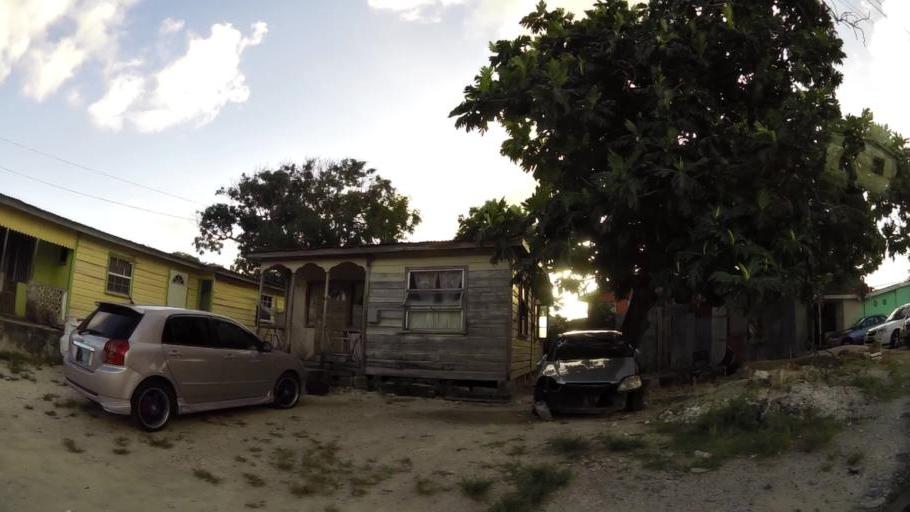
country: BB
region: Saint Philip
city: Crane
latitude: 13.1105
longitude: -59.4720
